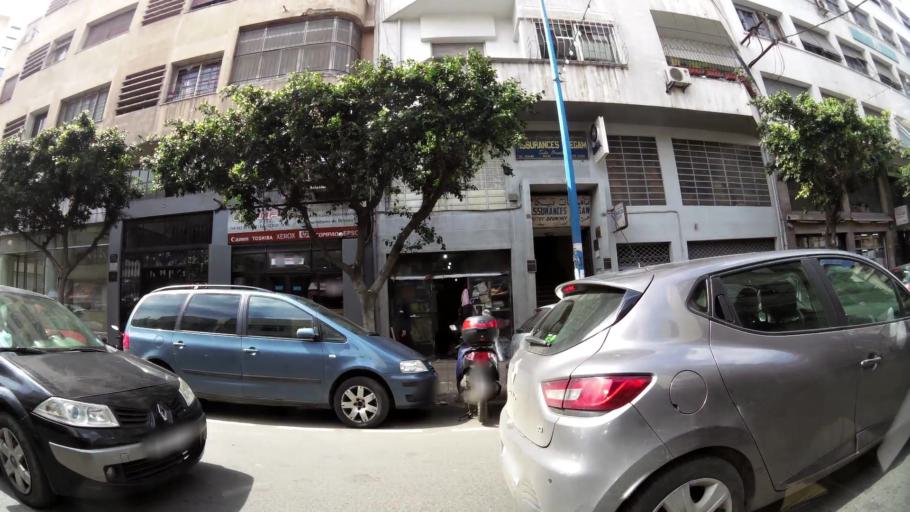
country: MA
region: Grand Casablanca
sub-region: Casablanca
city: Casablanca
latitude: 33.5897
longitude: -7.6110
